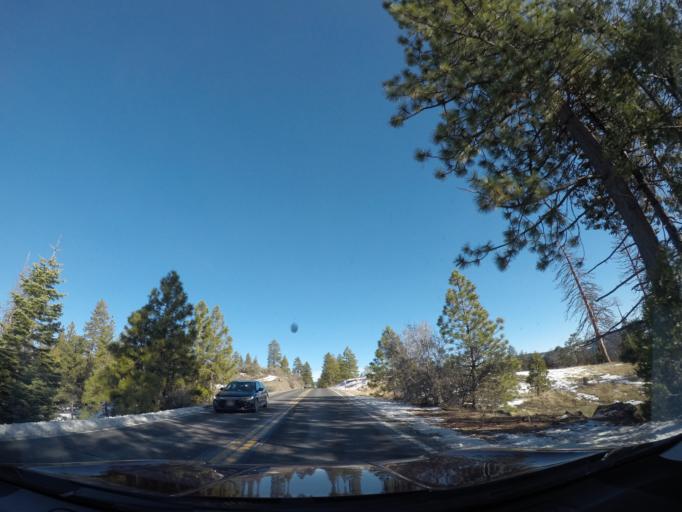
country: US
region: California
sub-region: Tuolumne County
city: Twain Harte
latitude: 38.1473
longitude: -120.0798
